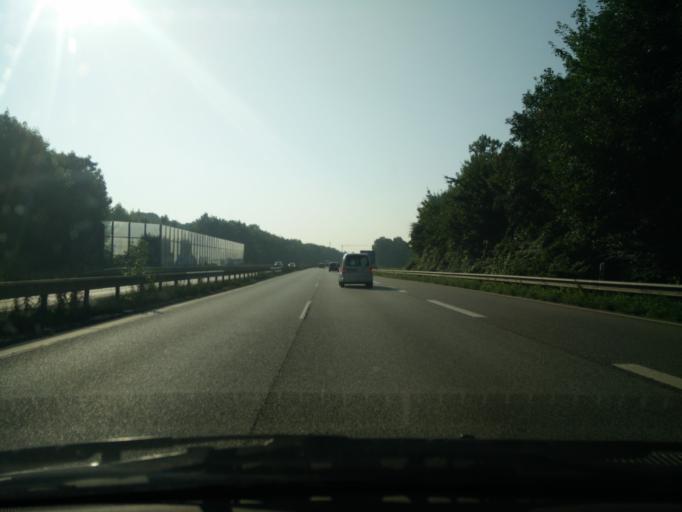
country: DE
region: Schleswig-Holstein
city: Rellingen
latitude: 53.6475
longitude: 9.8264
